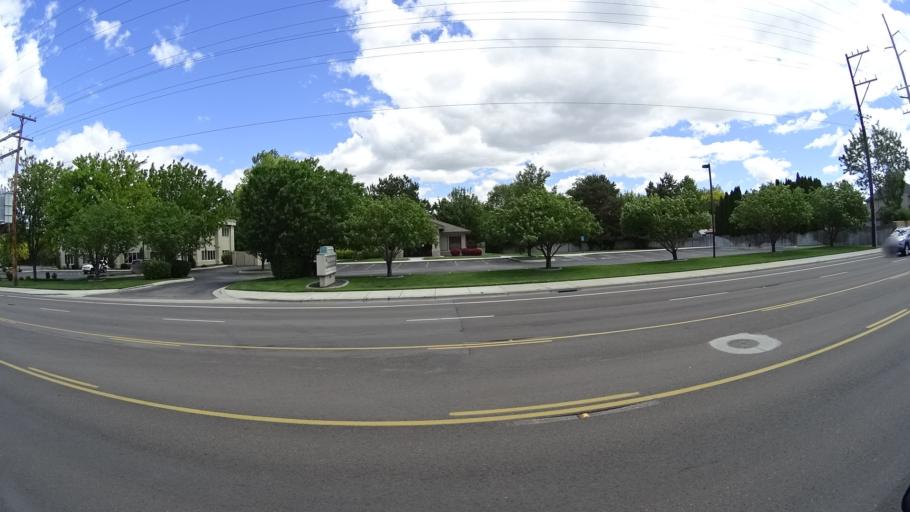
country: US
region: Idaho
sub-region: Ada County
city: Eagle
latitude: 43.6469
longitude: -116.3345
